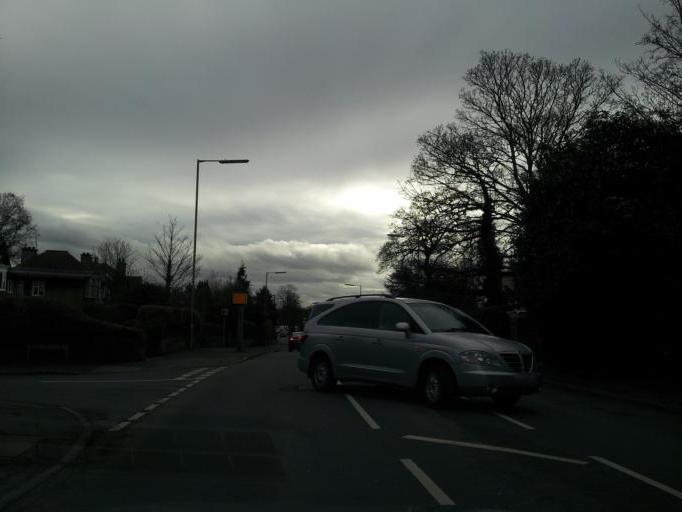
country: GB
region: England
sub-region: Staffordshire
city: Stafford
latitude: 52.7936
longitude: -2.1186
